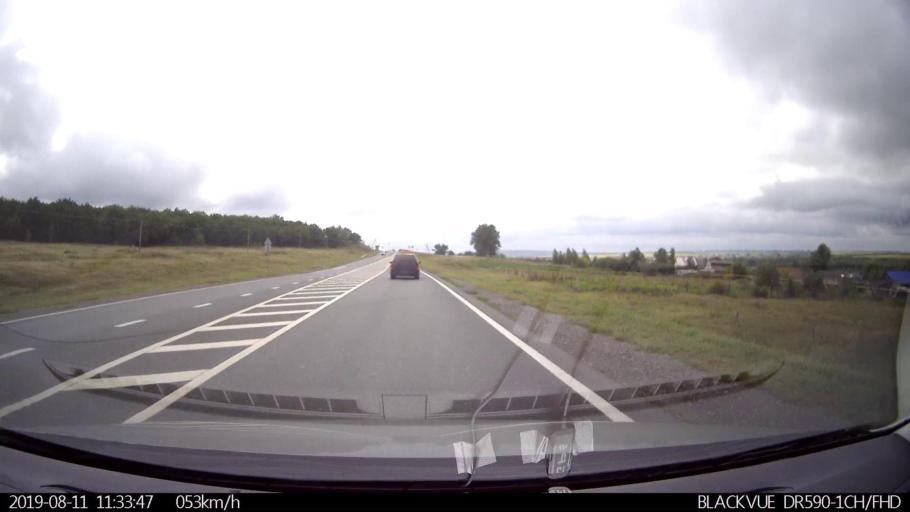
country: RU
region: Ulyanovsk
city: Silikatnyy
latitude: 54.0242
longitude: 48.2141
